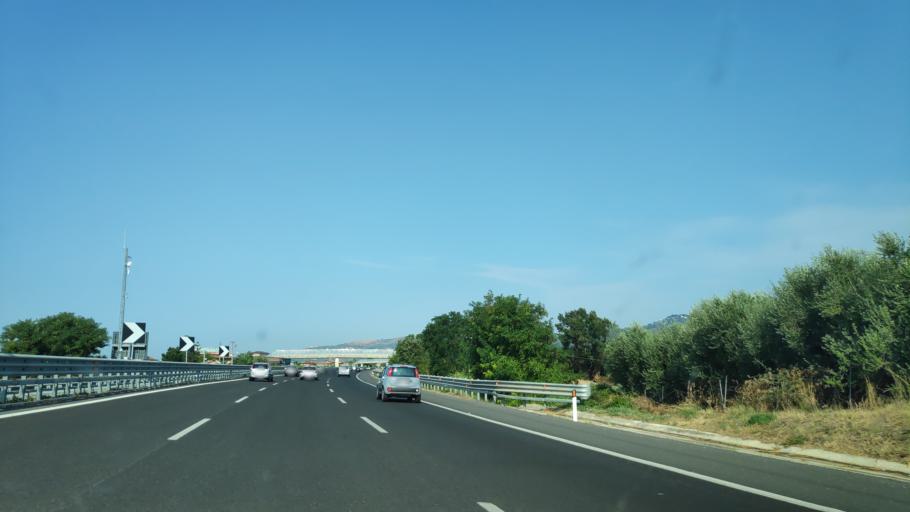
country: IT
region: Campania
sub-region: Provincia di Salerno
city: Quadrivio
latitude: 40.6062
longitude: 15.1028
